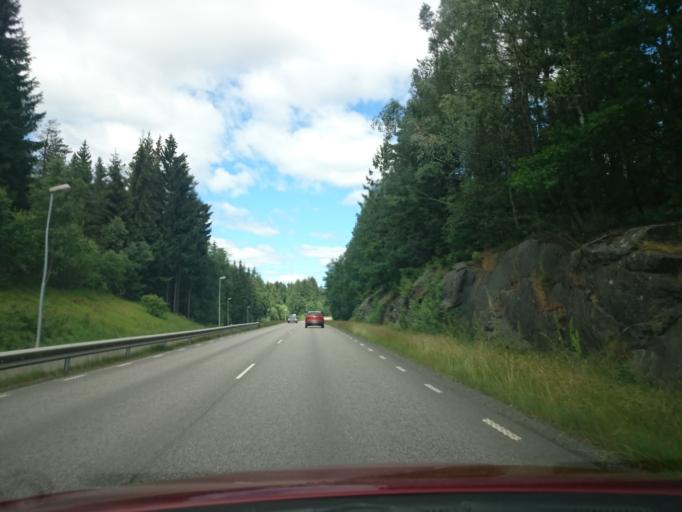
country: SE
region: Vaestra Goetaland
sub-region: Lerums Kommun
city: Grabo
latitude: 57.8231
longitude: 12.2952
